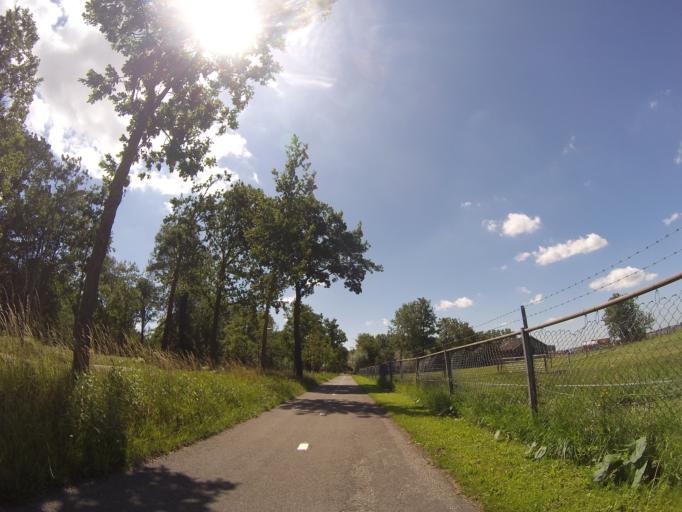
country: NL
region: Utrecht
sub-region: Stichtse Vecht
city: Spechtenkamp
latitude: 52.1242
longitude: 4.9836
